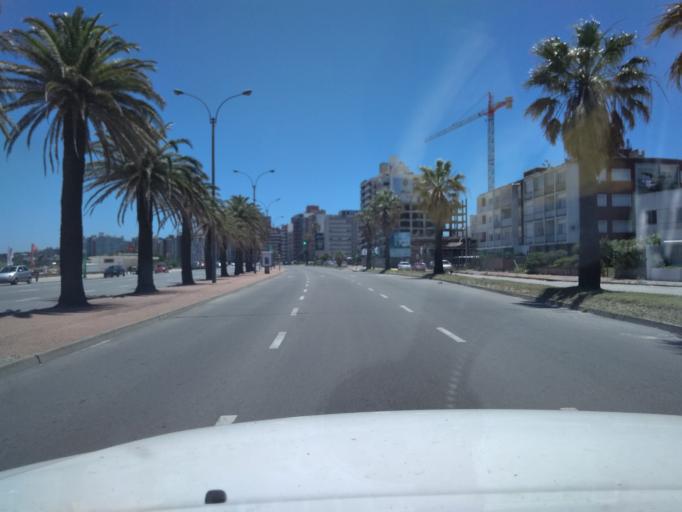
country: UY
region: Canelones
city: Paso de Carrasco
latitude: -34.8965
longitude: -56.1032
